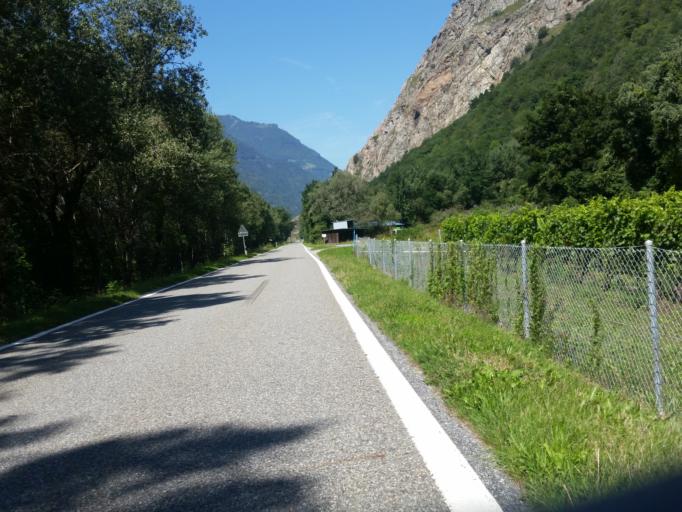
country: CH
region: Valais
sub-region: Saint-Maurice District
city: Vernayaz
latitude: 46.1365
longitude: 7.0542
